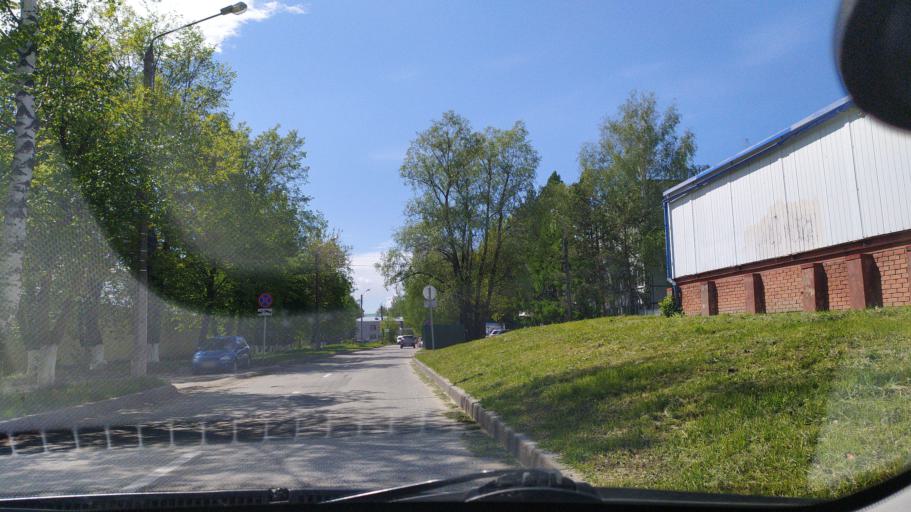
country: RU
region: Chuvashia
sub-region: Cheboksarskiy Rayon
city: Cheboksary
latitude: 56.1405
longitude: 47.2073
